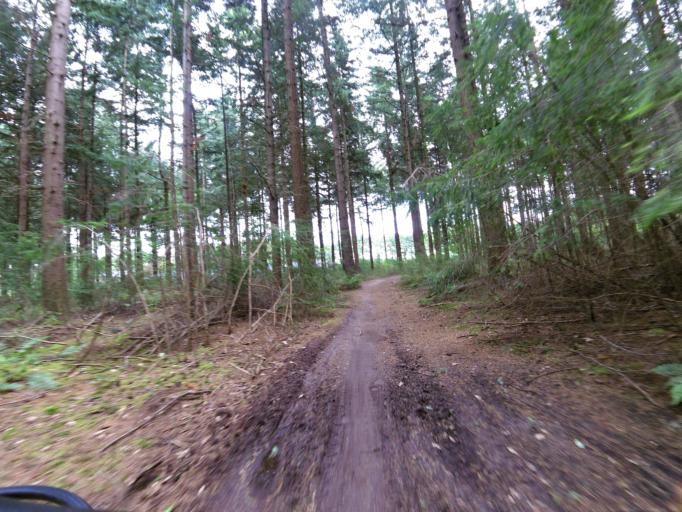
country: NL
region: North Brabant
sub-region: Gemeente Son en Breugel
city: Breugel
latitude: 51.5566
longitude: 5.5167
